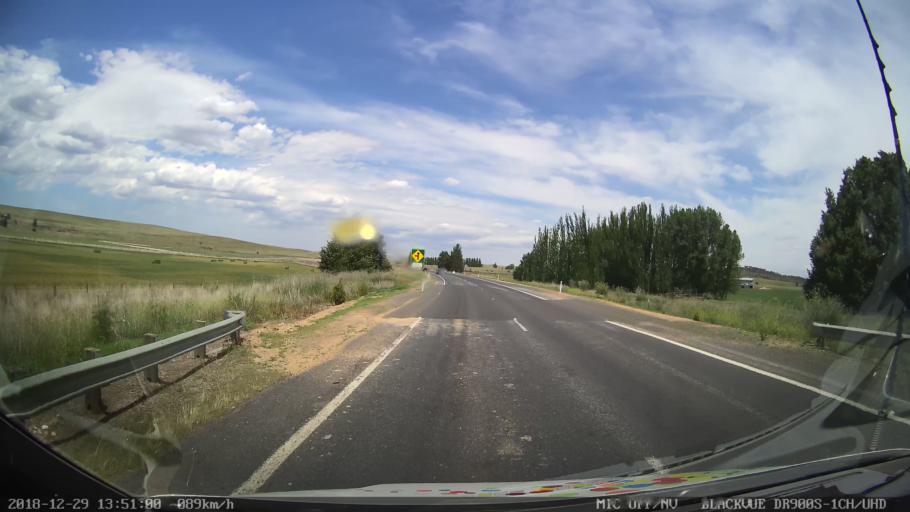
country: AU
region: New South Wales
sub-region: Cooma-Monaro
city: Cooma
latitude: -36.1755
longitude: 149.1542
